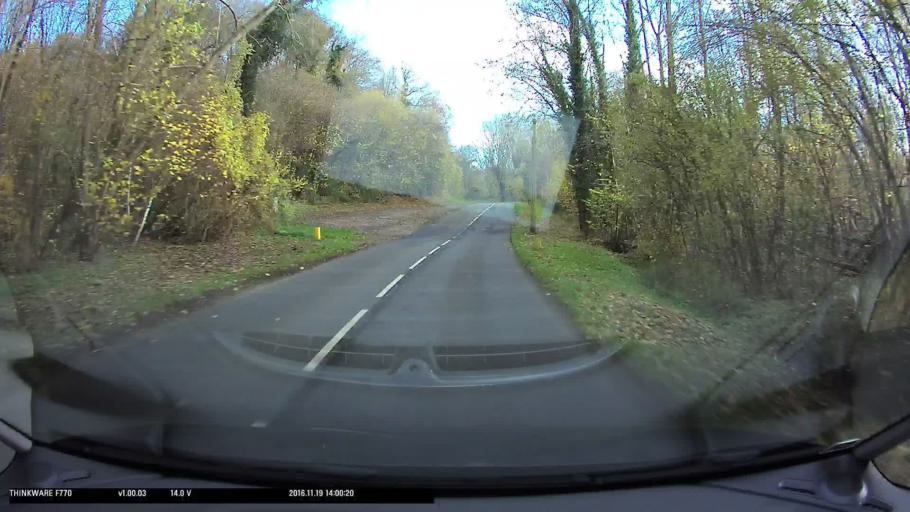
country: FR
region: Ile-de-France
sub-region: Departement du Val-d'Oise
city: Ableiges
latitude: 49.0879
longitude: 1.9928
